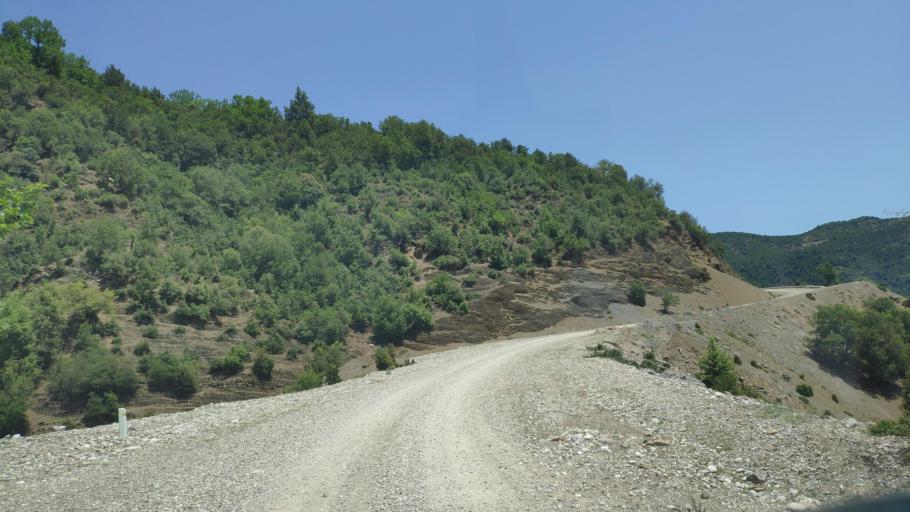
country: GR
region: Thessaly
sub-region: Nomos Kardhitsas
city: Anthiro
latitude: 39.1679
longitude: 21.3699
